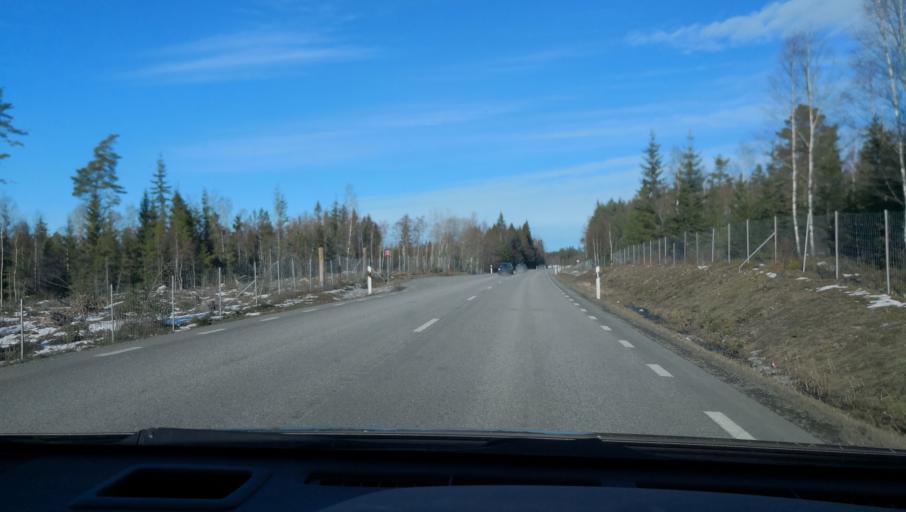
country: SE
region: Uppsala
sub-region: Uppsala Kommun
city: Vattholma
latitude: 60.0361
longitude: 17.7502
